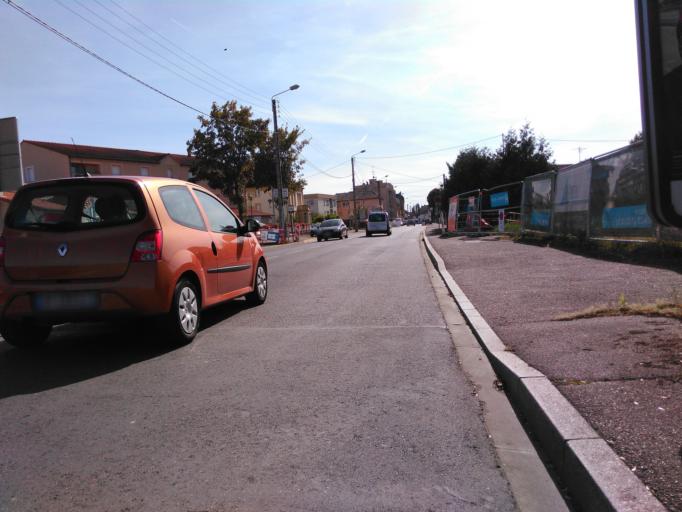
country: FR
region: Lorraine
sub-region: Departement de la Moselle
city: Thionville
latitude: 49.3725
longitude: 6.1693
